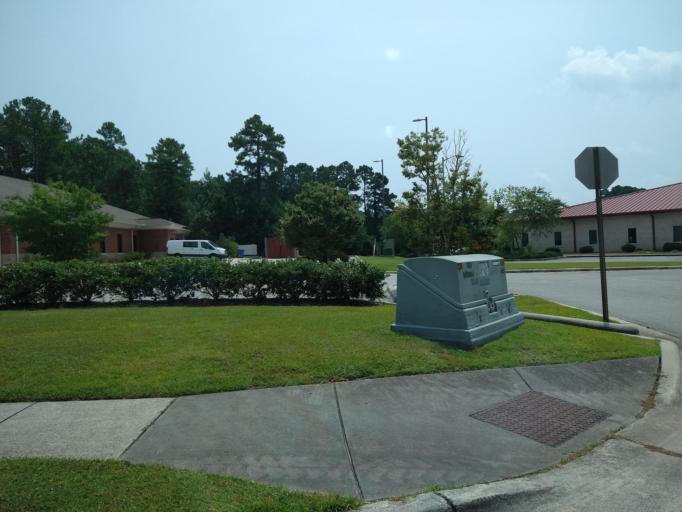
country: US
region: North Carolina
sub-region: Onslow County
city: Pumpkin Center
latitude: 34.7607
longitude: -77.3769
